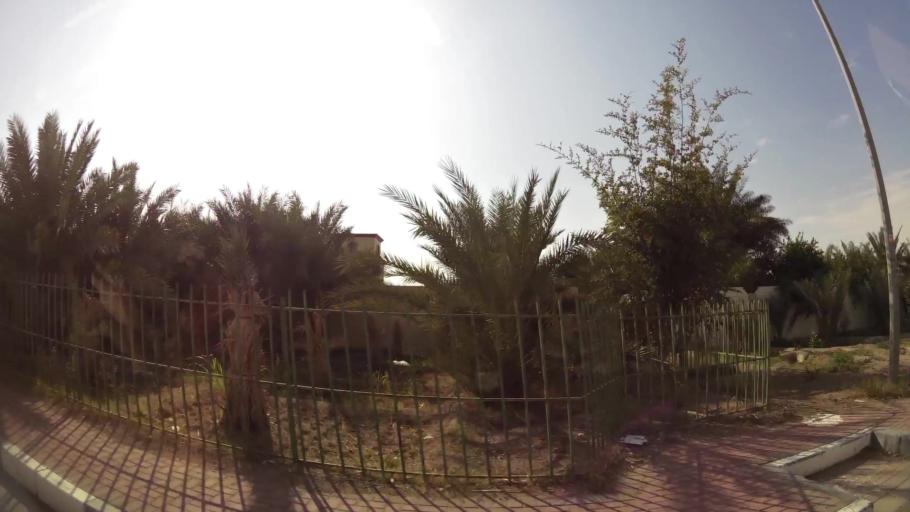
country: AE
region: Abu Dhabi
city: Al Ain
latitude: 24.0814
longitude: 55.8629
